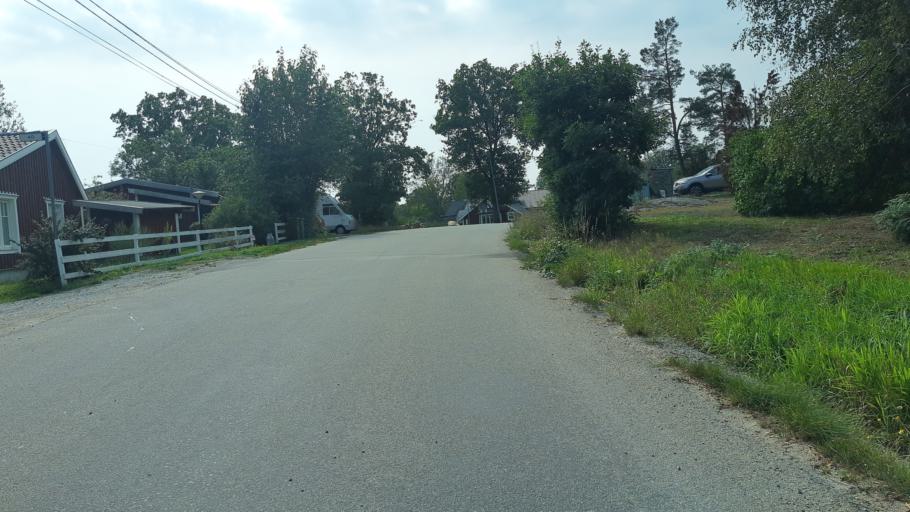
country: SE
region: Blekinge
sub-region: Karlskrona Kommun
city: Nattraby
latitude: 56.1822
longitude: 15.4984
